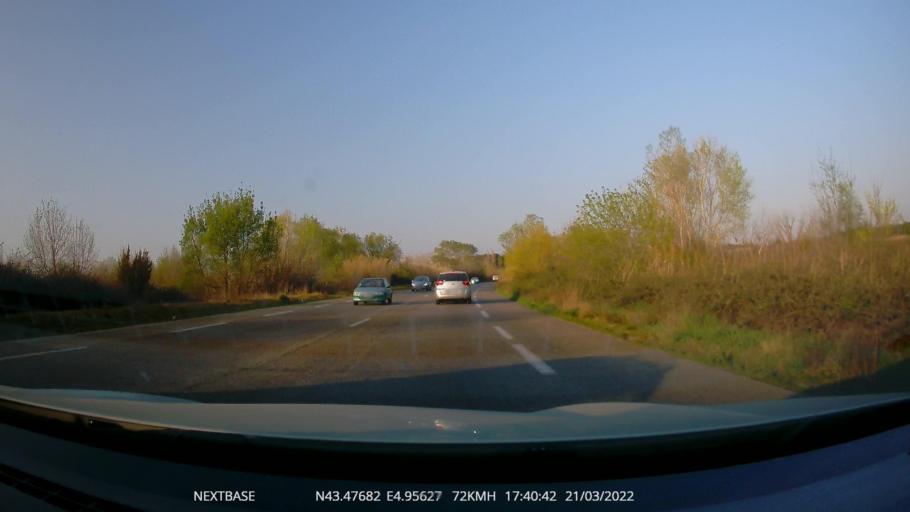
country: FR
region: Provence-Alpes-Cote d'Azur
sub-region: Departement des Bouches-du-Rhone
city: Fos-sur-Mer
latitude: 43.4771
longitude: 4.9564
